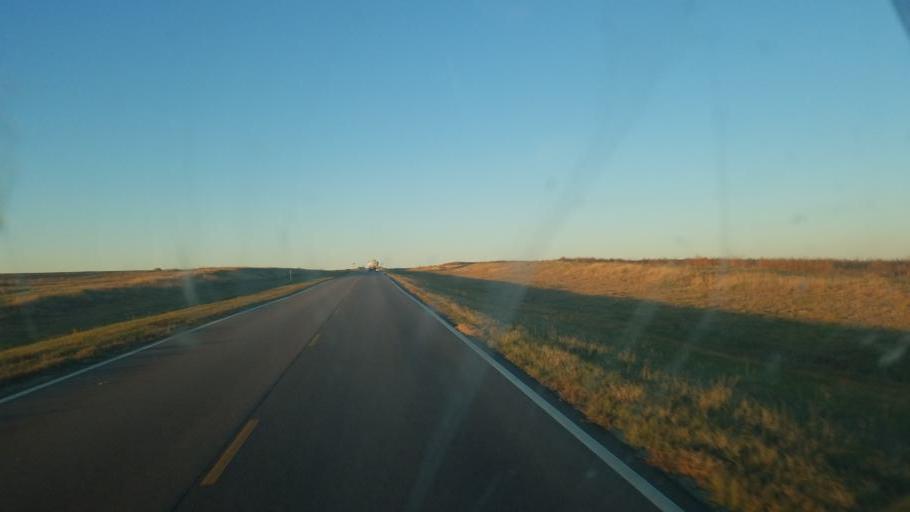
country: US
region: Kansas
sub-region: Wallace County
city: Sharon Springs
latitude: 38.8956
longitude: -101.8681
